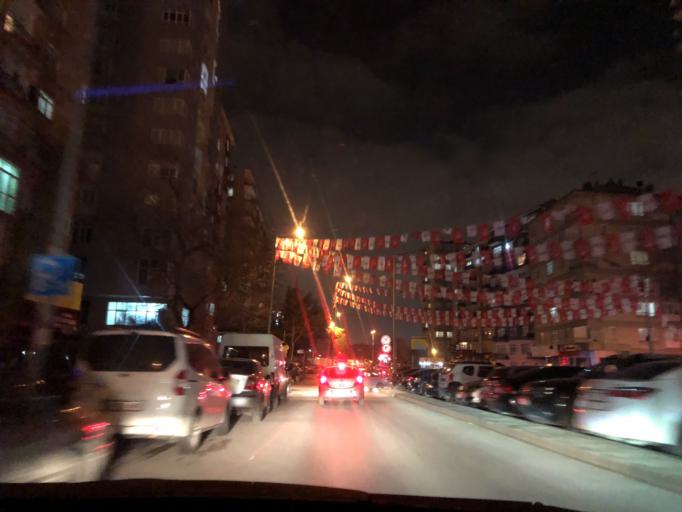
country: TR
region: Ankara
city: Batikent
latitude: 39.9651
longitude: 32.7956
